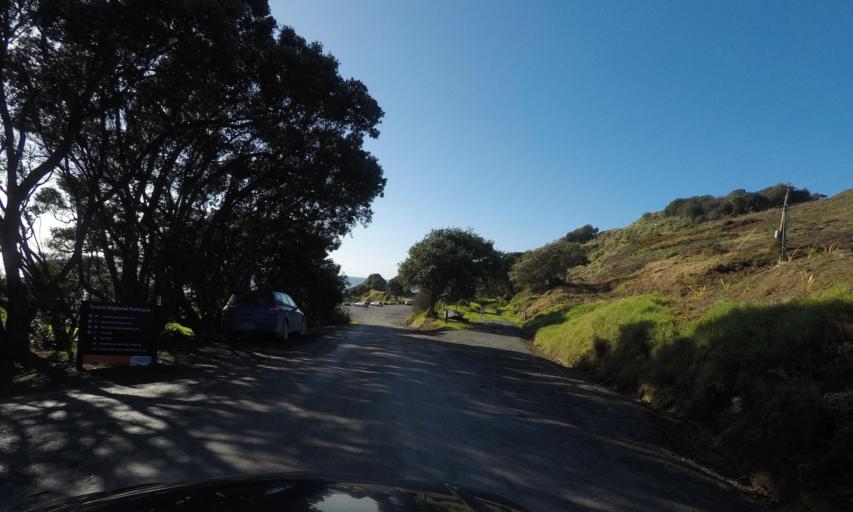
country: NZ
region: Auckland
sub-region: Auckland
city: Wellsford
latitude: -36.1603
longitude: 174.6460
